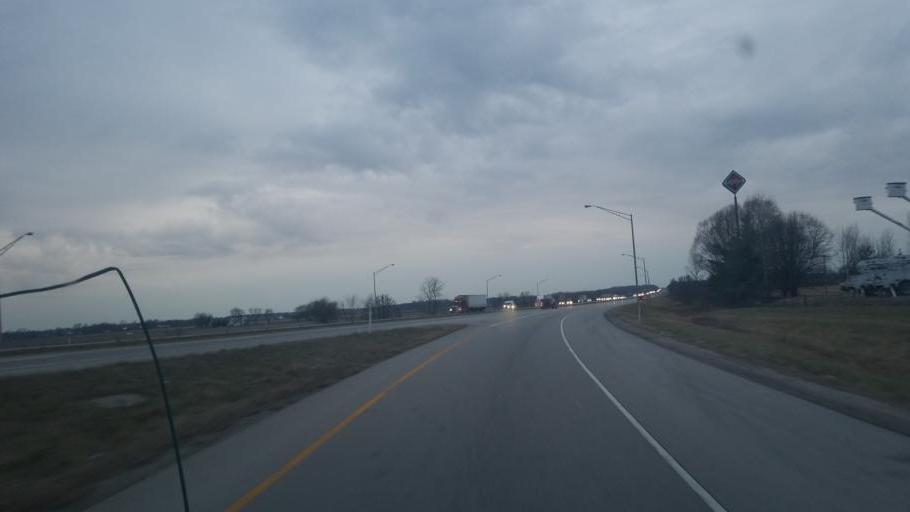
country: US
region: Indiana
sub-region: Clay County
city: Brazil
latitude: 39.4497
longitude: -87.1292
